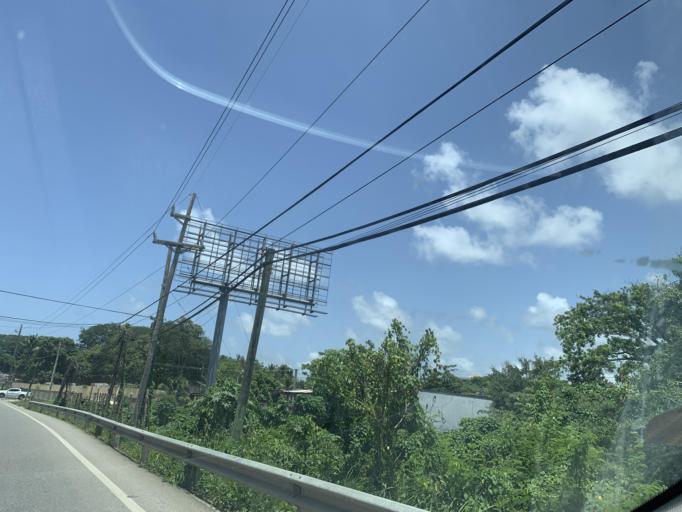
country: DO
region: Puerto Plata
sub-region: Puerto Plata
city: Puerto Plata
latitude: 19.7476
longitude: -70.5875
